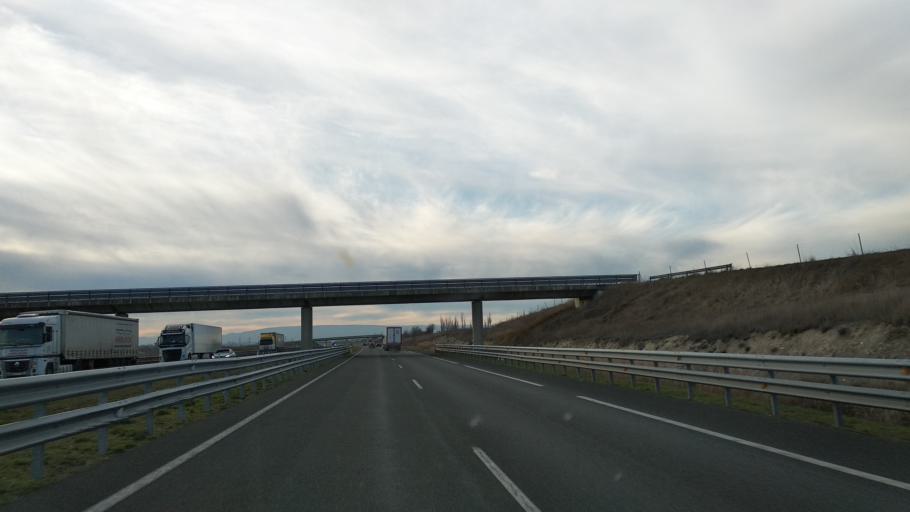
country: ES
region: Basque Country
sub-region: Provincia de Alava
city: Gasteiz / Vitoria
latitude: 42.8789
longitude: -2.5763
